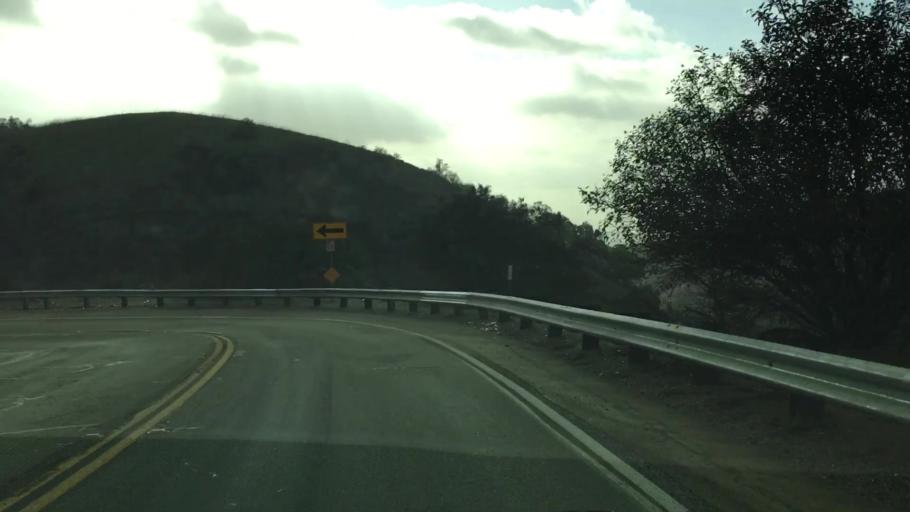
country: US
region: California
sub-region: Los Angeles County
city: Whittier
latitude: 33.9947
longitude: -118.0132
